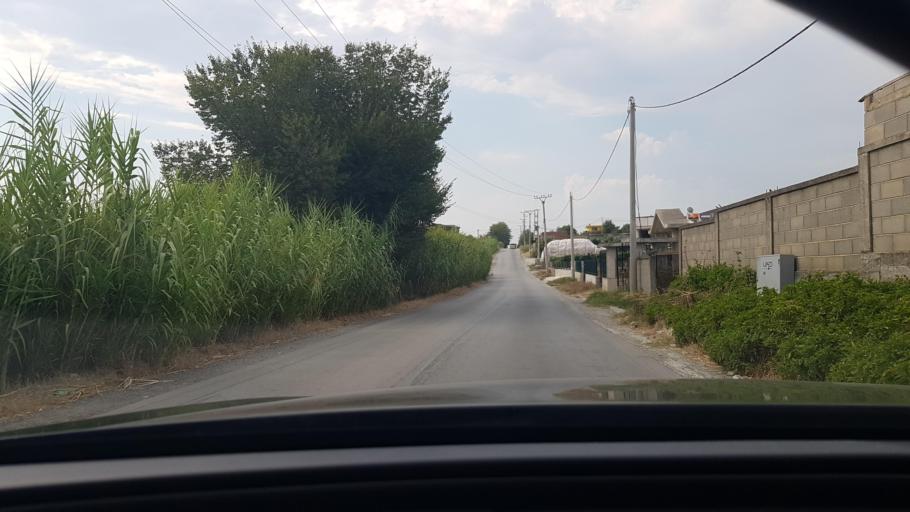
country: AL
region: Durres
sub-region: Rrethi i Durresit
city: Katundi i Ri
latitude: 41.4275
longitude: 19.5451
